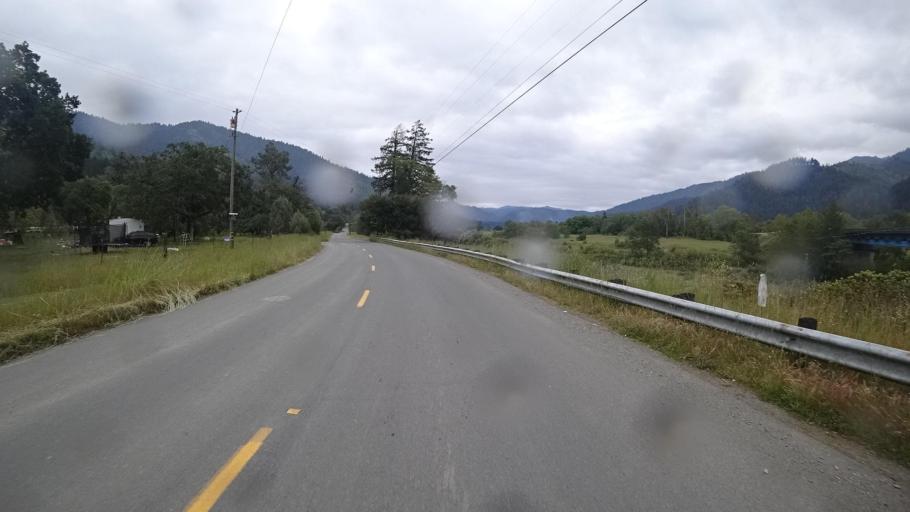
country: US
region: California
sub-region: Humboldt County
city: Willow Creek
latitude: 41.0621
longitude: -123.6849
